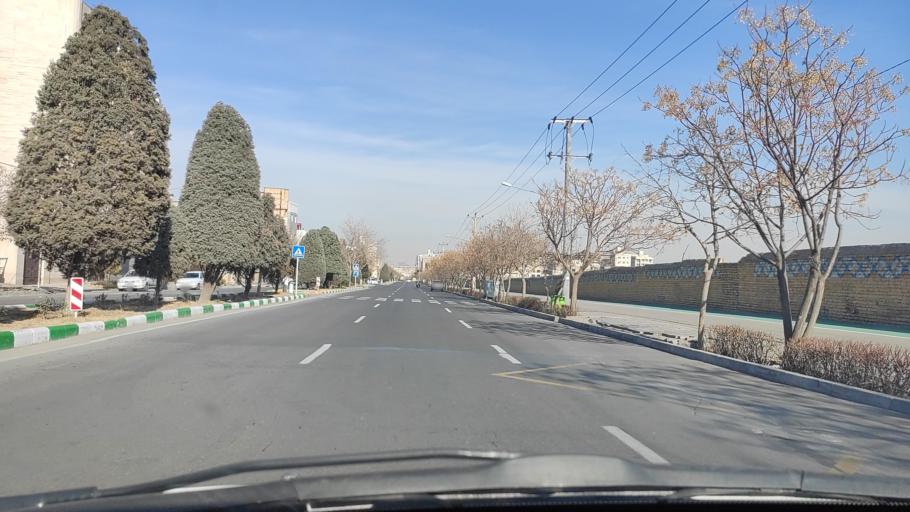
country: IR
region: Razavi Khorasan
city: Mashhad
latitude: 36.2857
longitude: 59.5316
